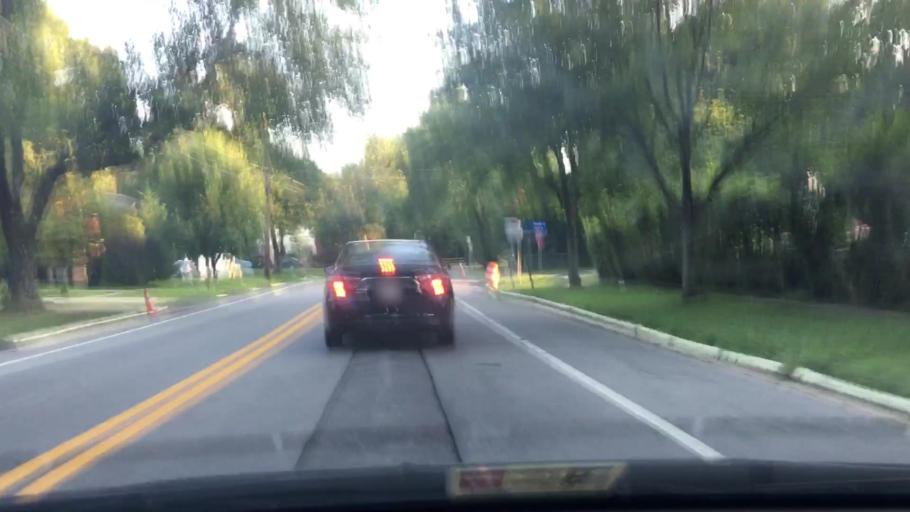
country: US
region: Maryland
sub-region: Montgomery County
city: North Bethesda
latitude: 39.0749
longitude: -77.1113
